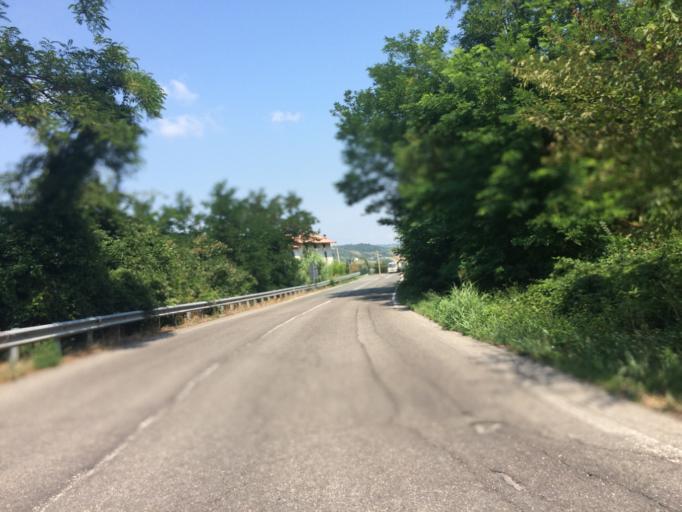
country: IT
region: Piedmont
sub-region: Provincia di Alessandria
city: Castelletto d'Erro
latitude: 44.6207
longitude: 8.4155
